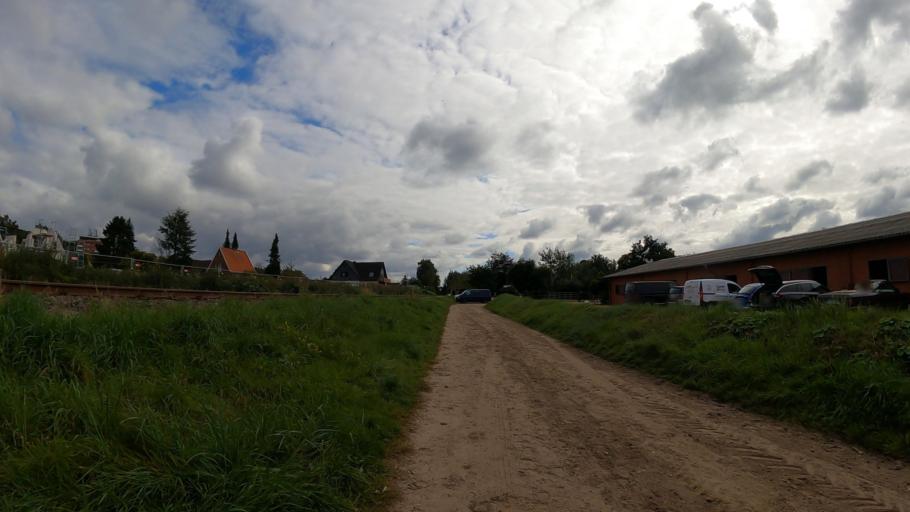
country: DE
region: Schleswig-Holstein
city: Geesthacht
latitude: 53.4505
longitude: 10.3531
